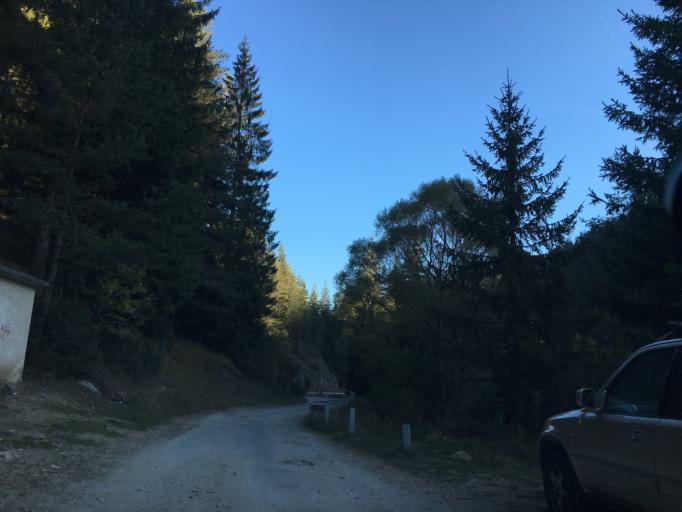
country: BG
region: Smolyan
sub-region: Obshtina Borino
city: Borino
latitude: 41.5885
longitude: 24.3858
